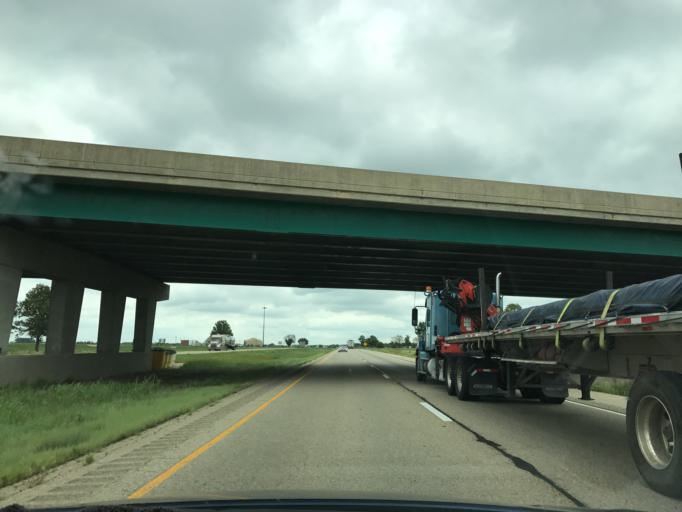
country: US
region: Illinois
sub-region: Bureau County
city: Ladd
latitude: 41.3677
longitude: -89.2198
